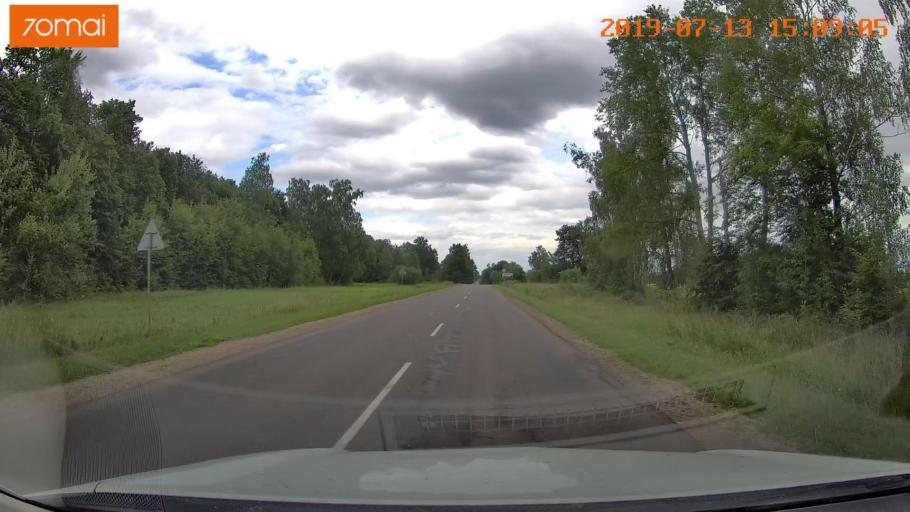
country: BY
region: Mogilev
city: Hlusha
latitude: 53.1742
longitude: 28.7565
